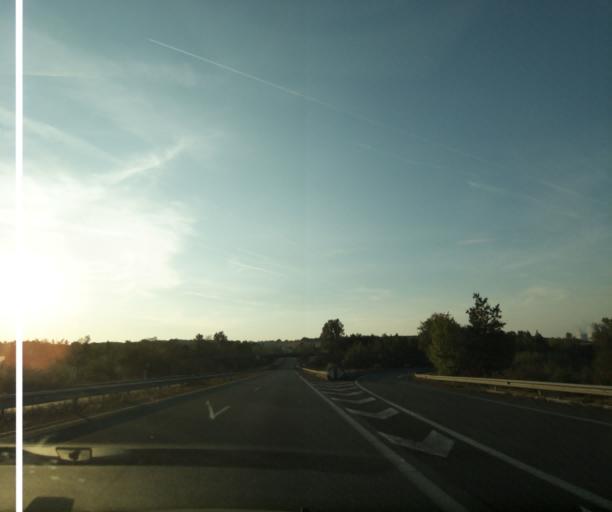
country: FR
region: Midi-Pyrenees
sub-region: Departement du Tarn-et-Garonne
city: Auvillar
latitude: 44.0614
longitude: 0.8647
